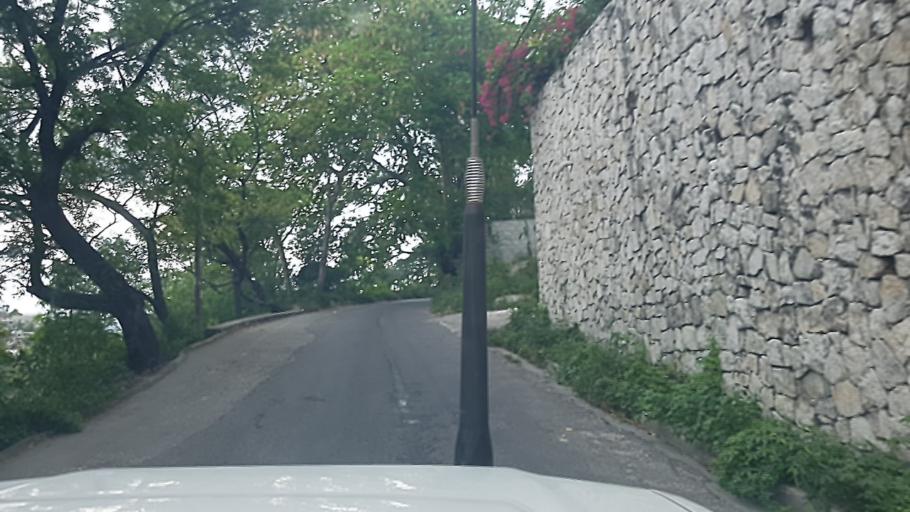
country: HT
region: Ouest
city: Petionville
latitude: 18.5261
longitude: -72.2982
